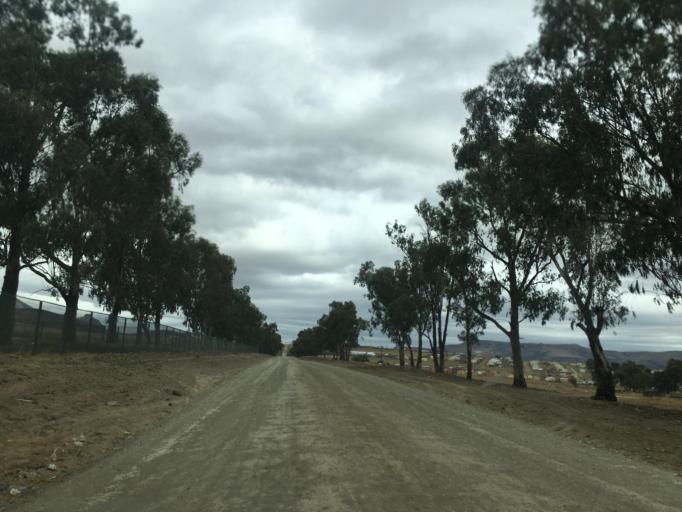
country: ZA
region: Eastern Cape
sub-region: Chris Hani District Municipality
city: Cala
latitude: -31.5352
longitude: 27.6888
